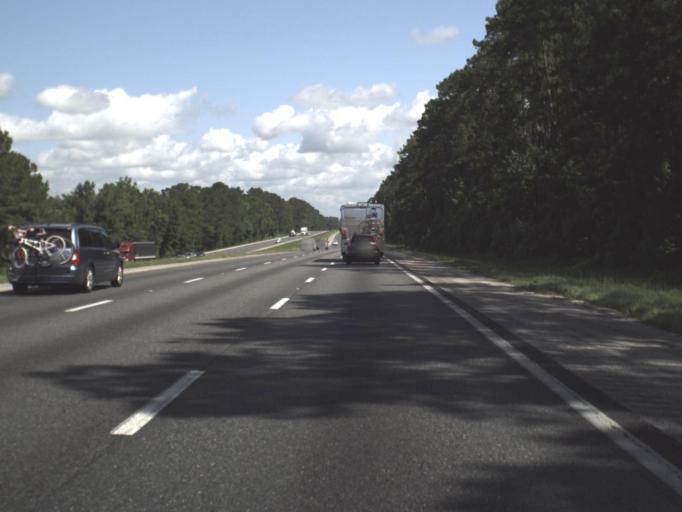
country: US
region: Florida
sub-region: Alachua County
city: Alachua
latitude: 29.7067
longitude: -82.4606
